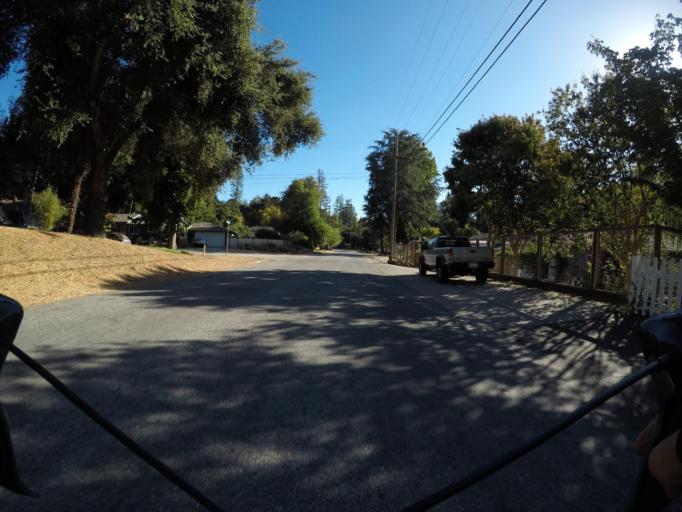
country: US
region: California
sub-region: Santa Cruz County
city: Ben Lomond
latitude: 37.0898
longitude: -122.0762
